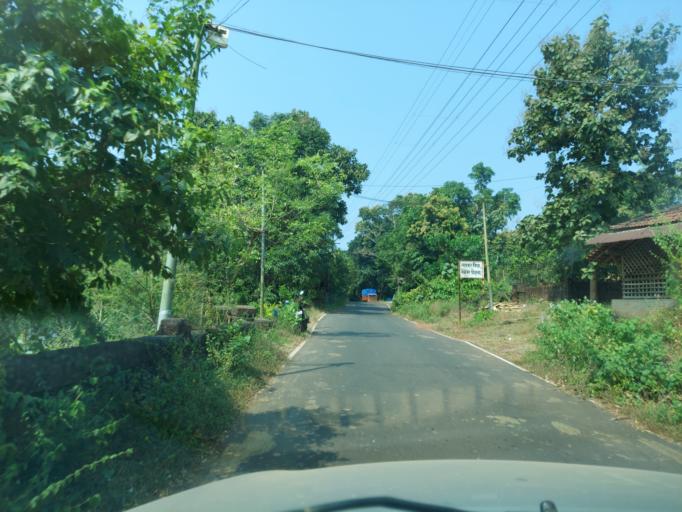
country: IN
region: Maharashtra
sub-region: Sindhudurg
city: Malvan
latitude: 15.9884
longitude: 73.5289
